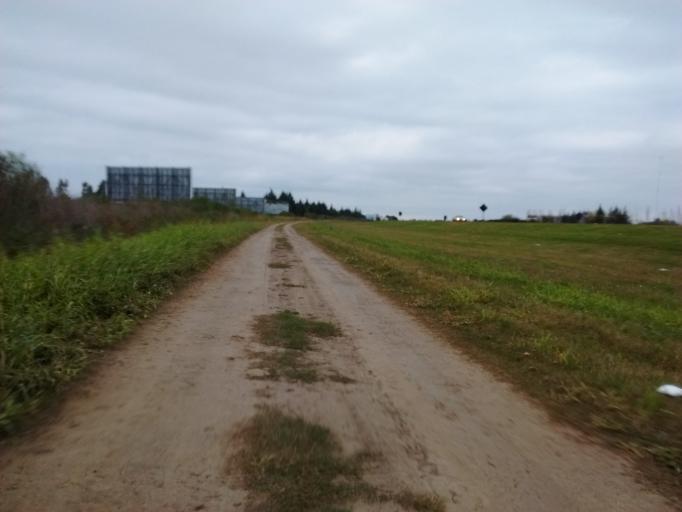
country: AR
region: Santa Fe
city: Funes
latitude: -32.9337
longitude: -60.8356
